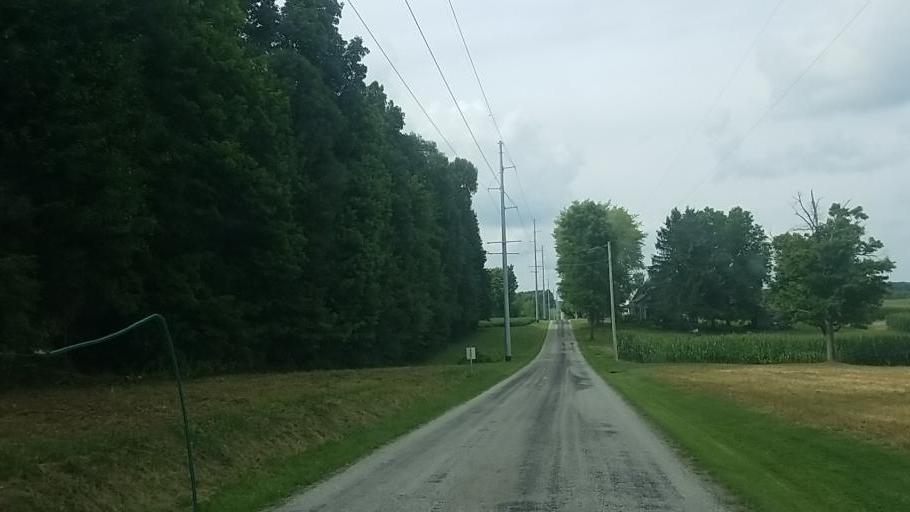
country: US
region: Ohio
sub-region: Sandusky County
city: Bellville
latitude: 40.5589
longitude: -82.5475
